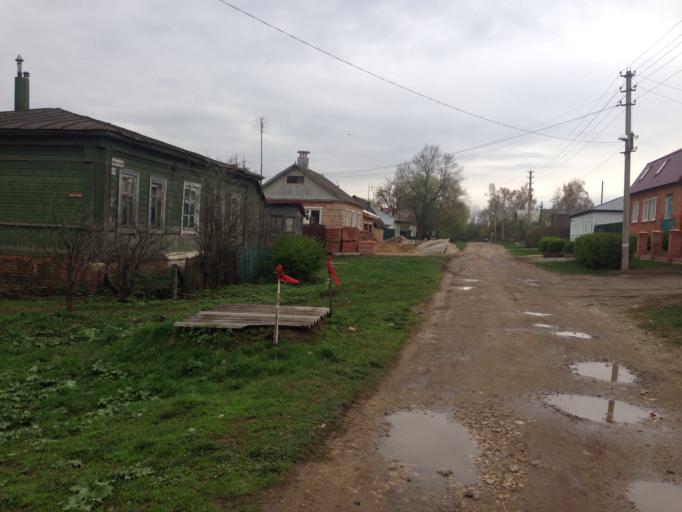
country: RU
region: Tula
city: Krapivna
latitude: 53.9379
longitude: 37.1512
